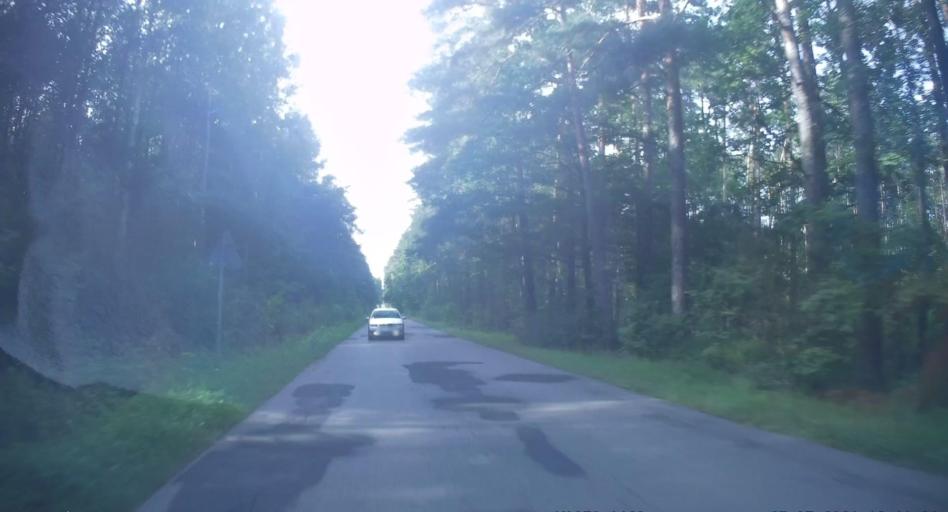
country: PL
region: Swietokrzyskie
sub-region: Powiat konecki
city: Konskie
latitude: 51.2292
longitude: 20.3833
